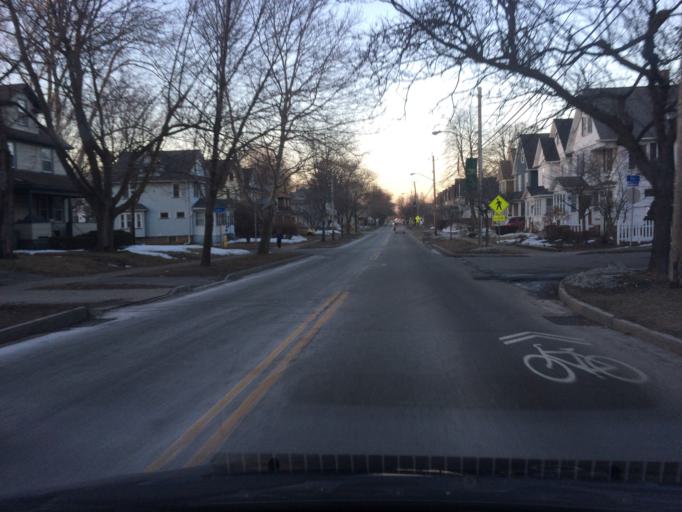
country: US
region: New York
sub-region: Monroe County
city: Rochester
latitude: 43.1353
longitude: -77.5986
